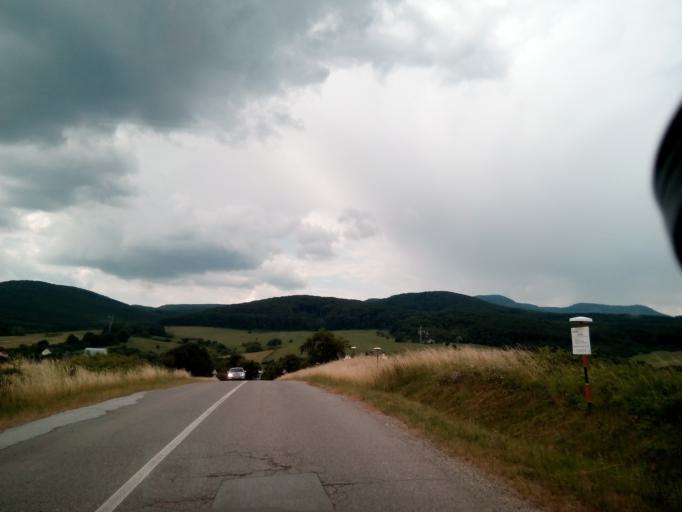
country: SK
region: Kosicky
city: Secovce
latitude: 48.6184
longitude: 21.5237
